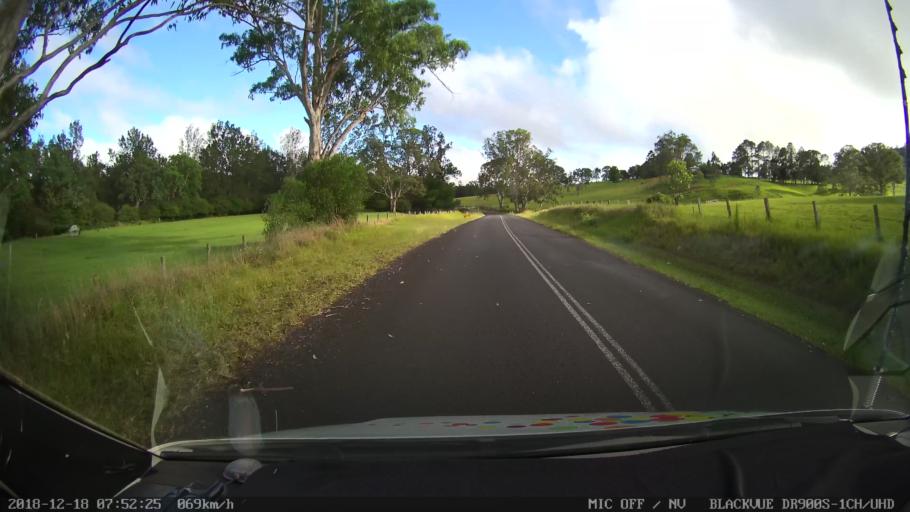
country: AU
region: New South Wales
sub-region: Kyogle
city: Kyogle
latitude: -28.4286
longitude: 152.5809
